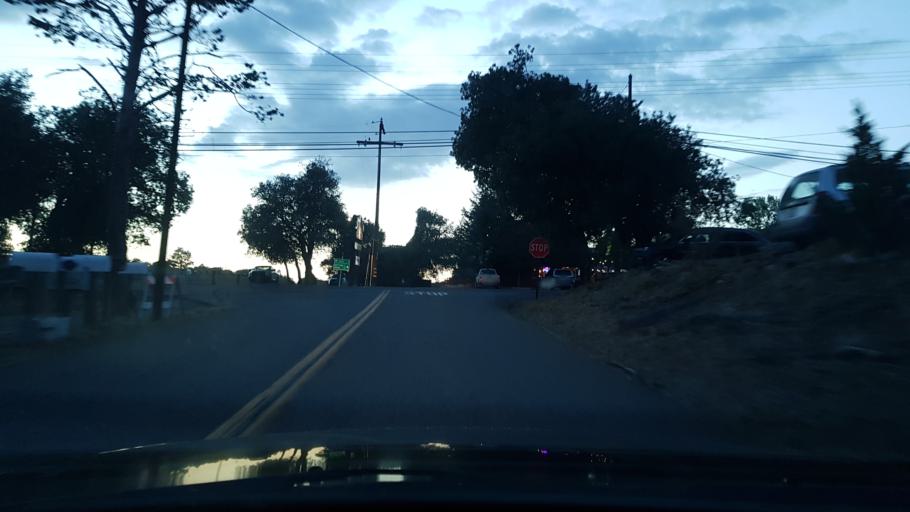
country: US
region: California
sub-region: San Diego County
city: Julian
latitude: 33.0944
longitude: -116.6455
